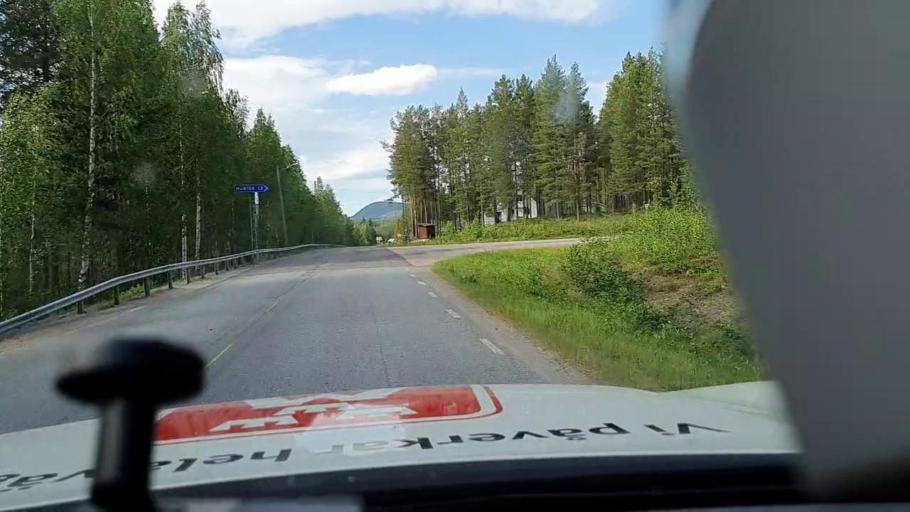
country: SE
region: Norrbotten
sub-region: Gallivare Kommun
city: Gaellivare
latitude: 66.4569
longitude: 20.6546
